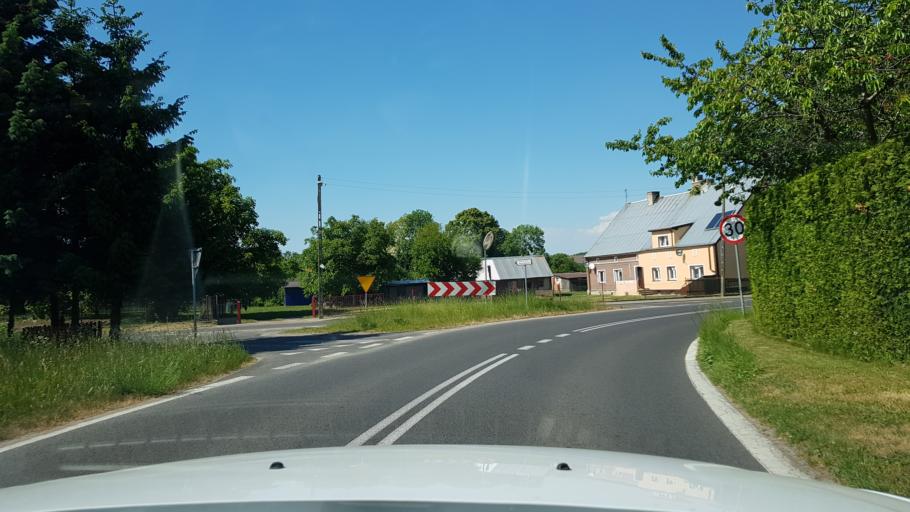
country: PL
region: West Pomeranian Voivodeship
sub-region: Powiat gryfinski
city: Banie
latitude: 53.0798
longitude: 14.6137
